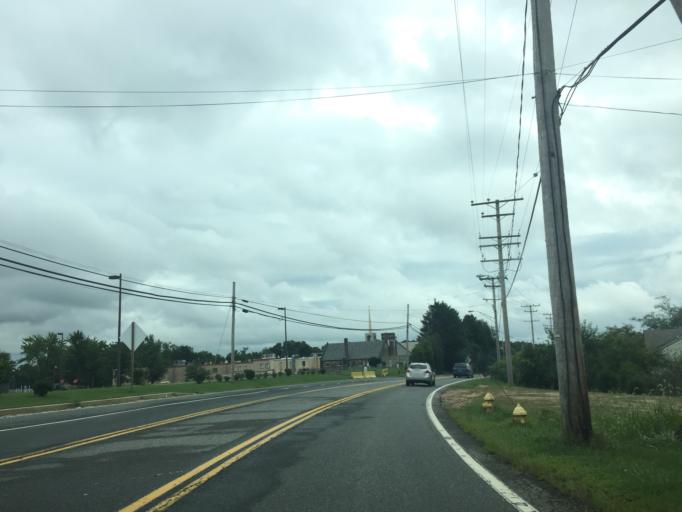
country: US
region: Maryland
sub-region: Harford County
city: Joppatowne
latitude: 39.4390
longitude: -76.3423
